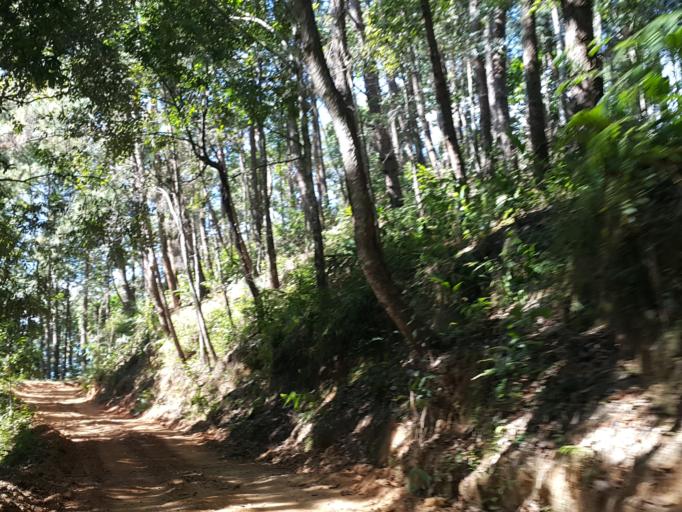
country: TH
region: Chiang Mai
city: Wiang Haeng
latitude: 19.5243
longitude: 98.8106
